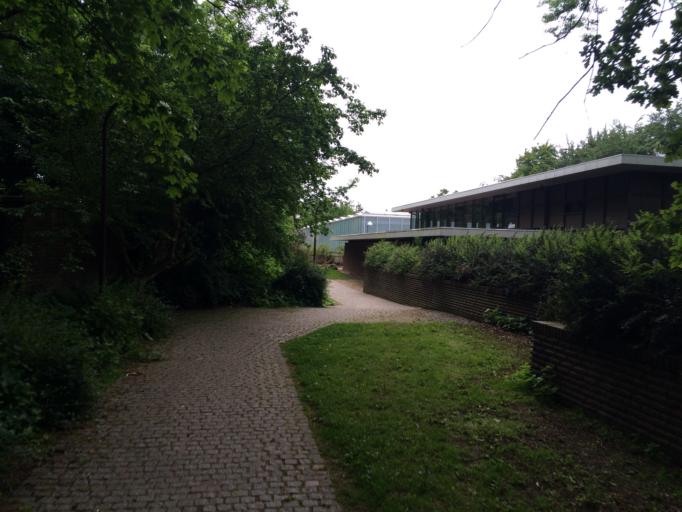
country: DK
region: Capital Region
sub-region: Gentofte Kommune
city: Charlottenlund
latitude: 55.7465
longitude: 12.5505
